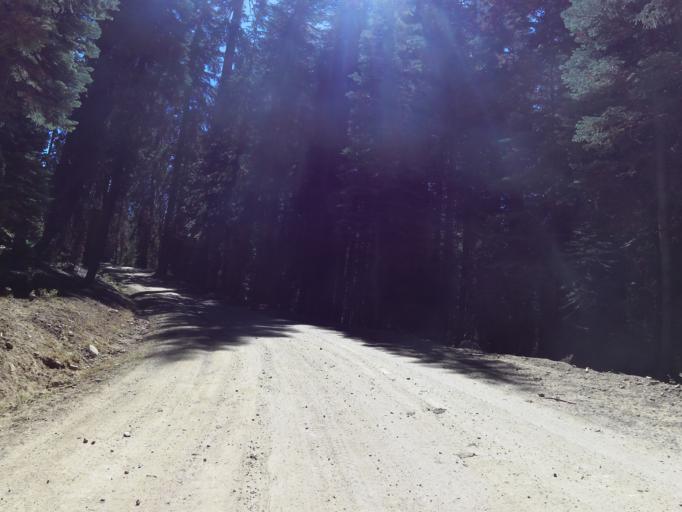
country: US
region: California
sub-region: Madera County
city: Oakhurst
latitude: 37.4316
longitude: -119.5034
